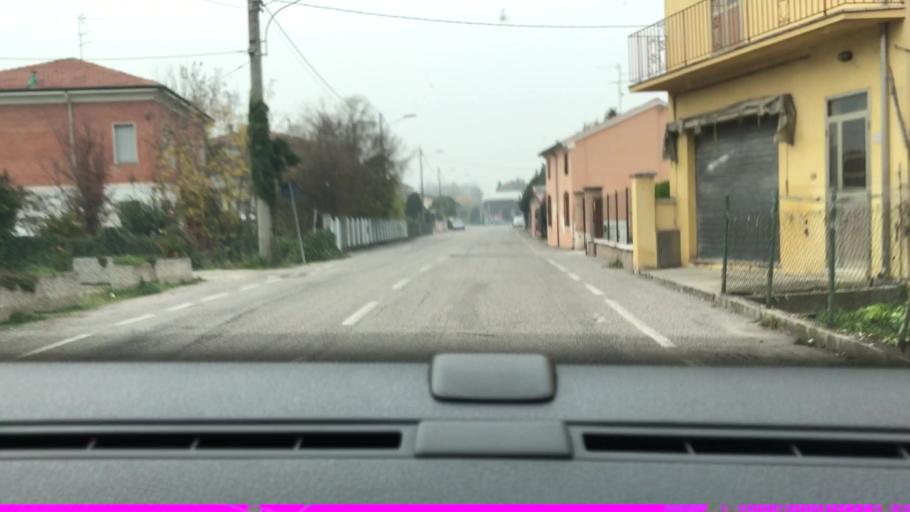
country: IT
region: Lombardy
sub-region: Provincia di Mantova
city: San Giacomo delle Segnate
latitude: 44.9723
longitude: 11.0319
